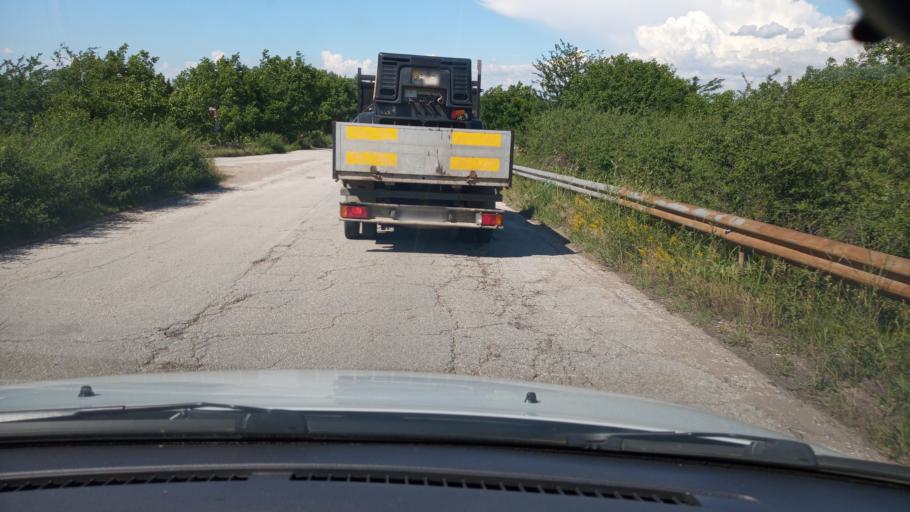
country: BG
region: Pleven
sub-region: Obshtina Dolna Mitropoliya
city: Dolna Mitropoliya
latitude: 43.4403
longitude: 24.5262
